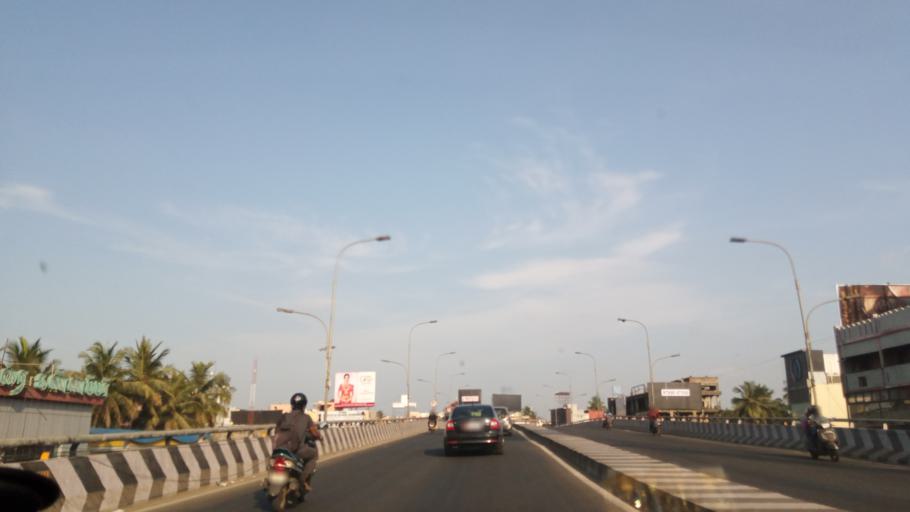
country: IN
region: Tamil Nadu
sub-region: Thiruvallur
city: Porur
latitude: 13.0352
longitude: 80.1552
